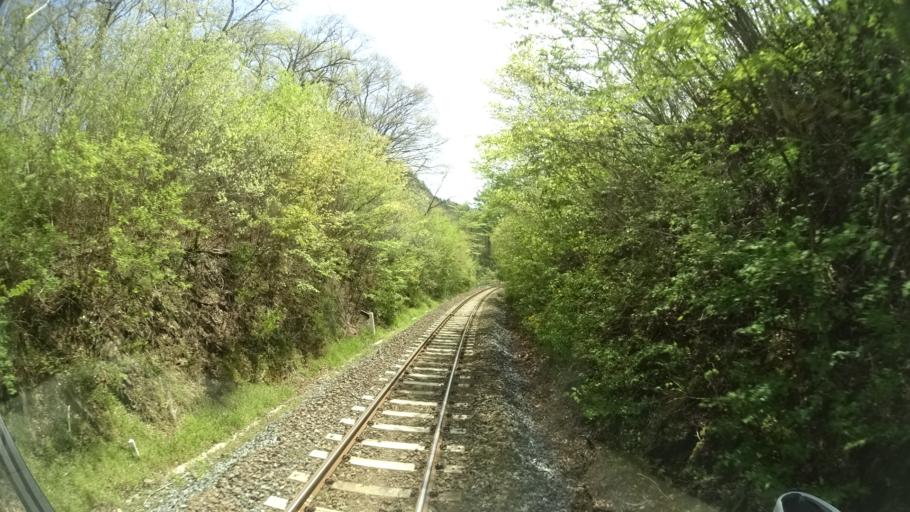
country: JP
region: Iwate
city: Ofunato
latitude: 38.9152
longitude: 141.5049
